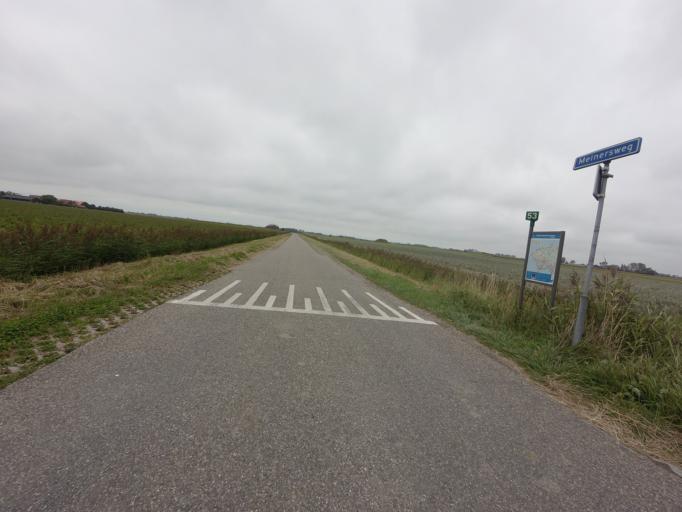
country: NL
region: Zeeland
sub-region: Gemeente Middelburg
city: Middelburg
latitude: 51.4914
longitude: 3.5668
